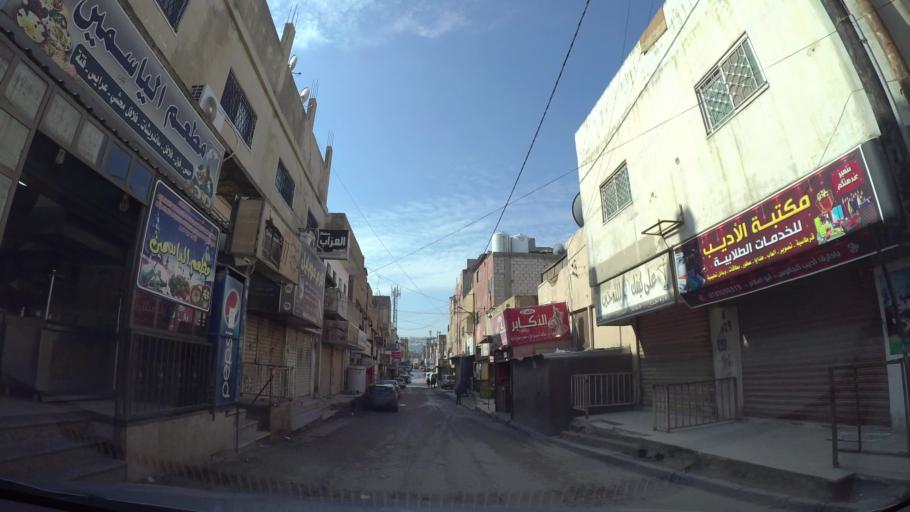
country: JO
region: Amman
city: Al Jubayhah
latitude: 32.0690
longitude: 35.8403
